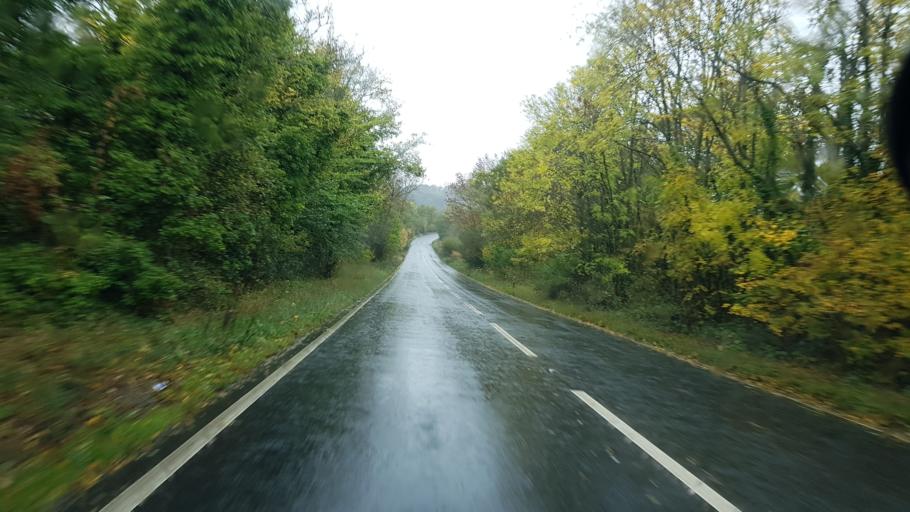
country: GB
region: England
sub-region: Gloucestershire
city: Stow on the Wold
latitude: 51.9080
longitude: -1.7193
